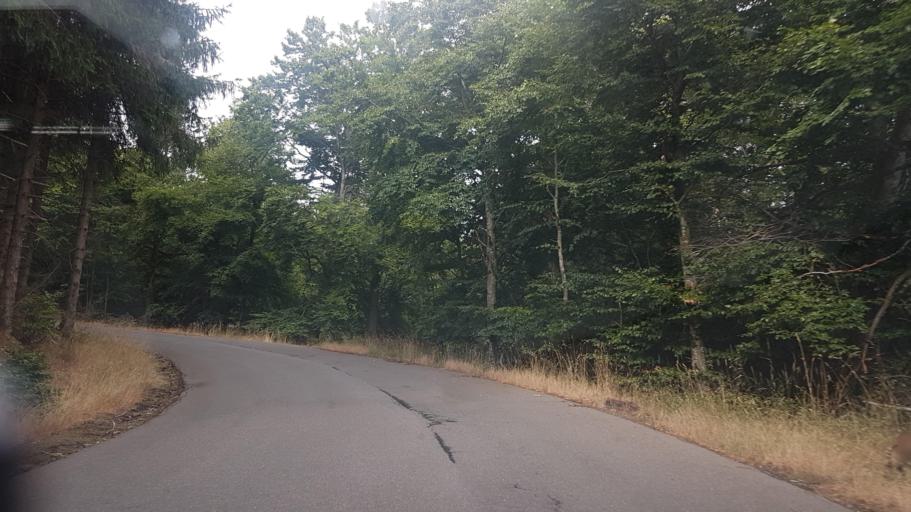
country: DE
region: Rheinland-Pfalz
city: Borfink
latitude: 49.7315
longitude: 7.0985
